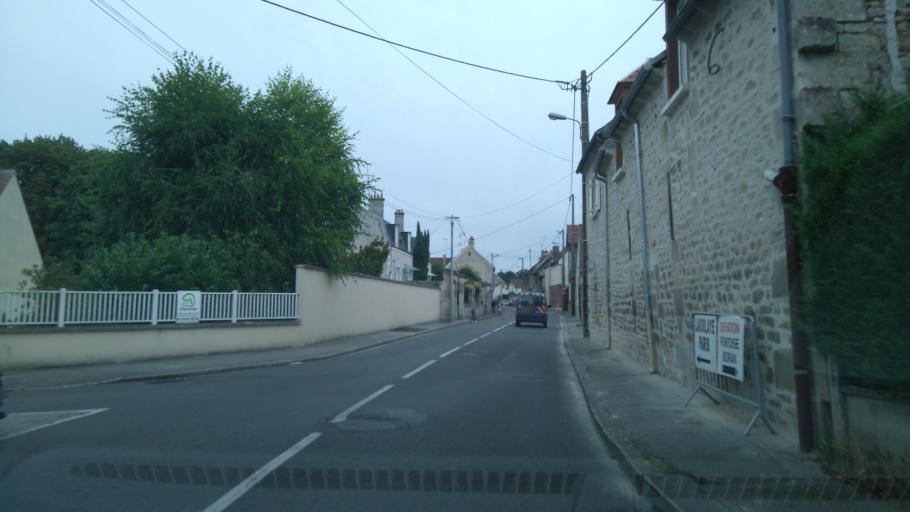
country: FR
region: Picardie
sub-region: Departement de l'Oise
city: Gouvieux
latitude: 49.1861
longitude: 2.4076
